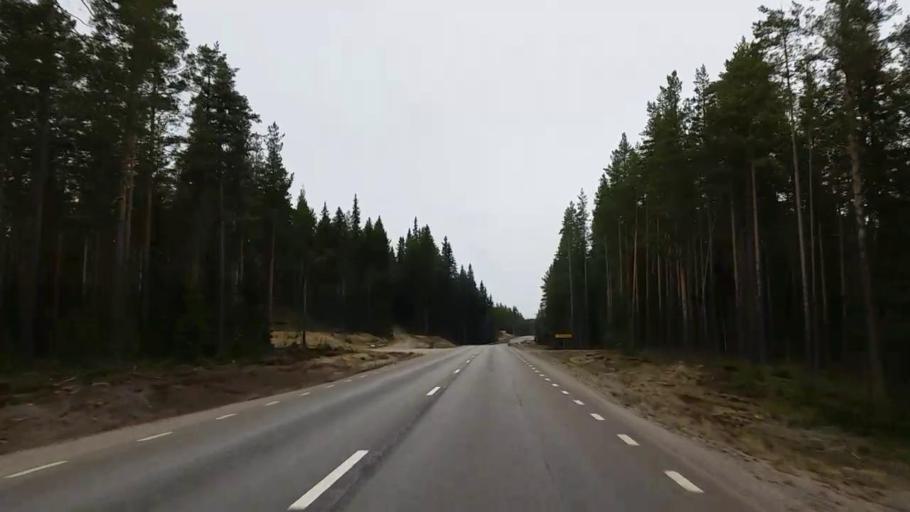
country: SE
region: Gaevleborg
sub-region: Ovanakers Kommun
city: Edsbyn
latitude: 61.1667
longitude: 15.8825
